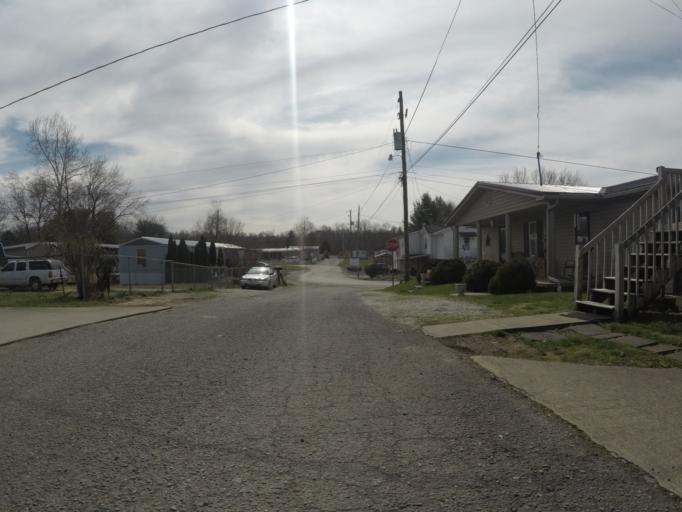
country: US
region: West Virginia
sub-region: Cabell County
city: Pea Ridge
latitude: 38.4184
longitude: -82.3518
